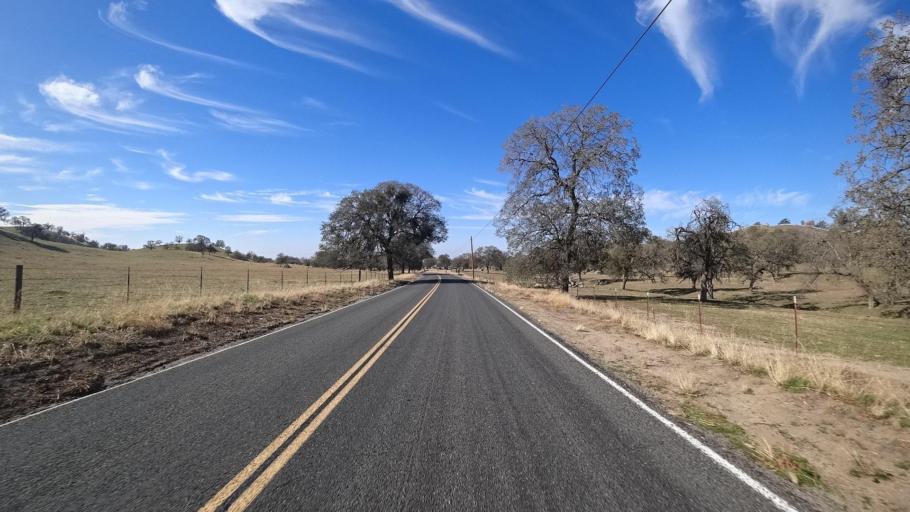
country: US
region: California
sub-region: Kern County
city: Oildale
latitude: 35.6273
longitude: -118.8356
